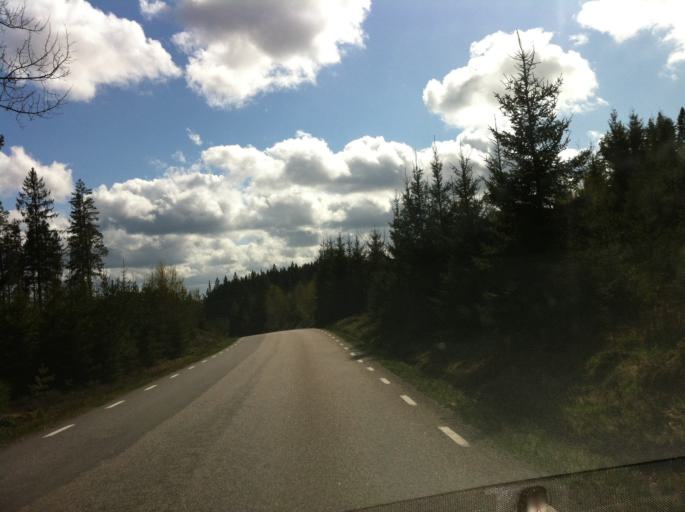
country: SE
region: Vaestra Goetaland
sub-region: Bollebygds Kommun
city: Bollebygd
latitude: 57.8120
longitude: 12.6401
